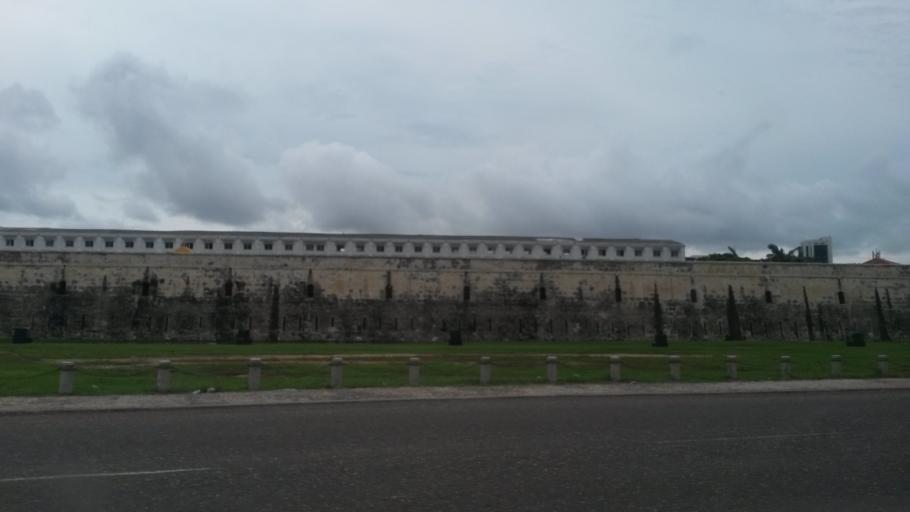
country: CO
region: Bolivar
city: Cartagena
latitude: 10.4306
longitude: -75.5470
